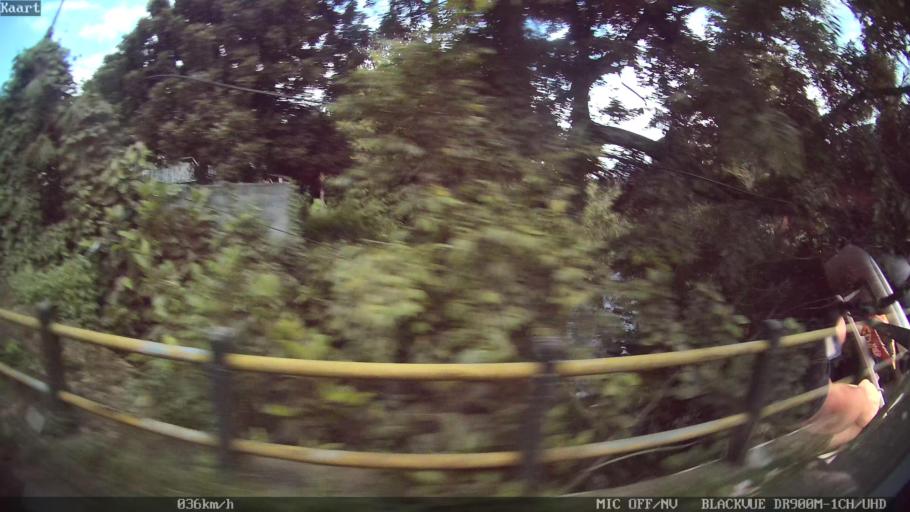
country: ID
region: Bali
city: Kauhan
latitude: -8.2722
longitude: 114.9700
